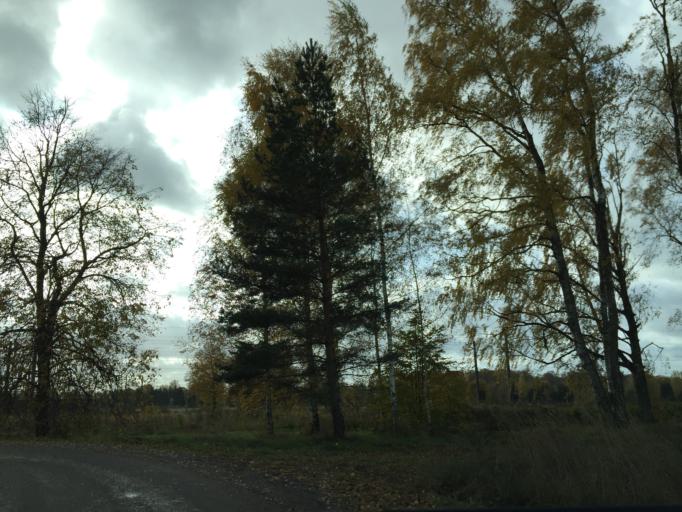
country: LV
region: Lielvarde
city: Lielvarde
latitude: 56.7159
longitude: 24.8477
